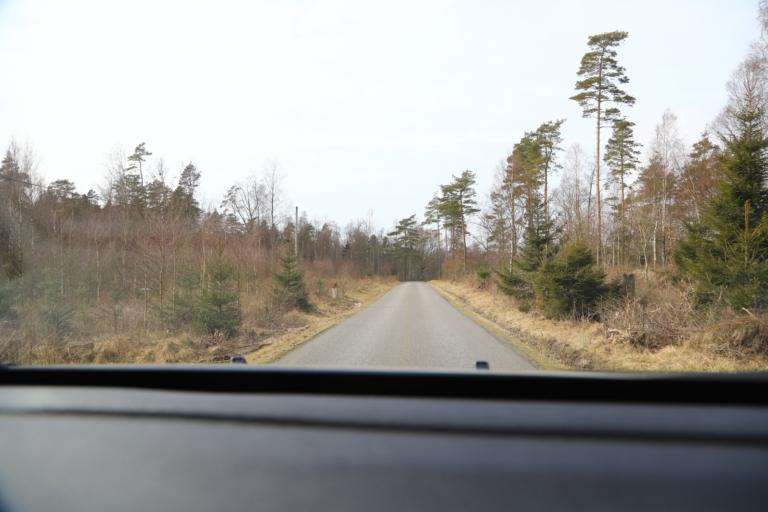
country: SE
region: Halland
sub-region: Varbergs Kommun
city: Veddige
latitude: 57.2153
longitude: 12.2443
